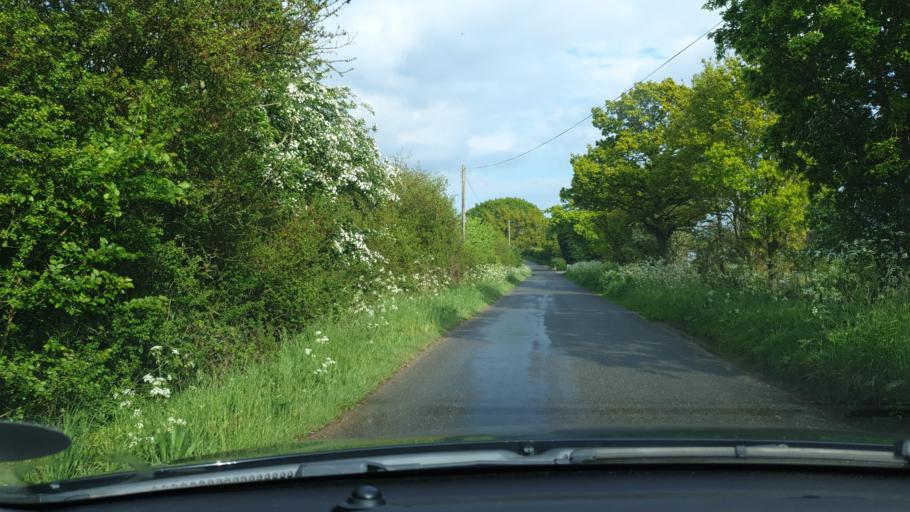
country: GB
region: England
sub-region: Essex
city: Saint Osyth
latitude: 51.8254
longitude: 1.0934
